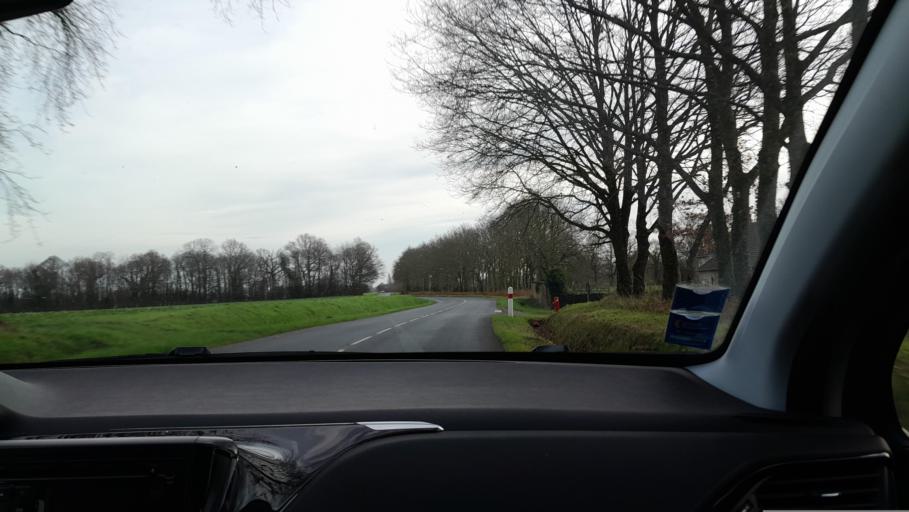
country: FR
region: Brittany
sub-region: Departement d'Ille-et-Vilaine
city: La Guerche-de-Bretagne
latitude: 47.9479
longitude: -1.2148
